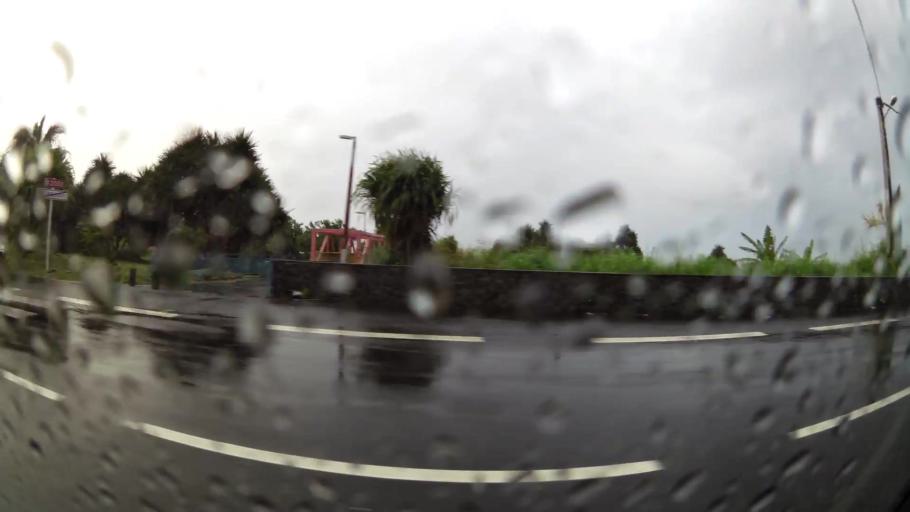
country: RE
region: Reunion
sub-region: Reunion
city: Saint-Benoit
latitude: -21.0267
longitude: 55.7060
